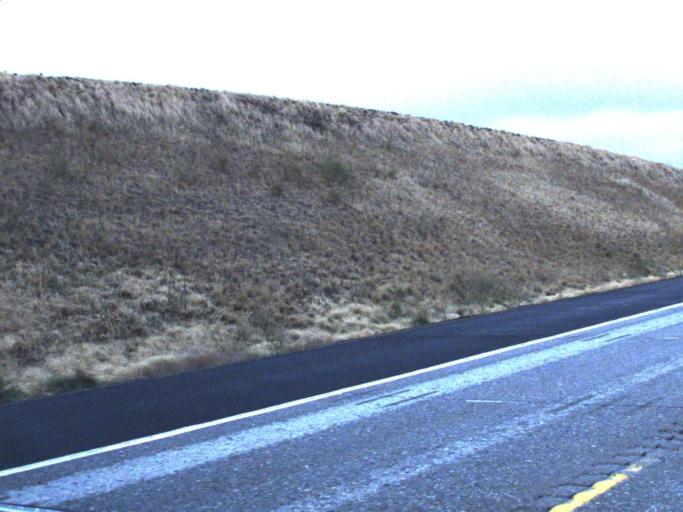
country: US
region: Washington
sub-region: Whitman County
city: Colfax
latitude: 47.0544
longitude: -117.3807
